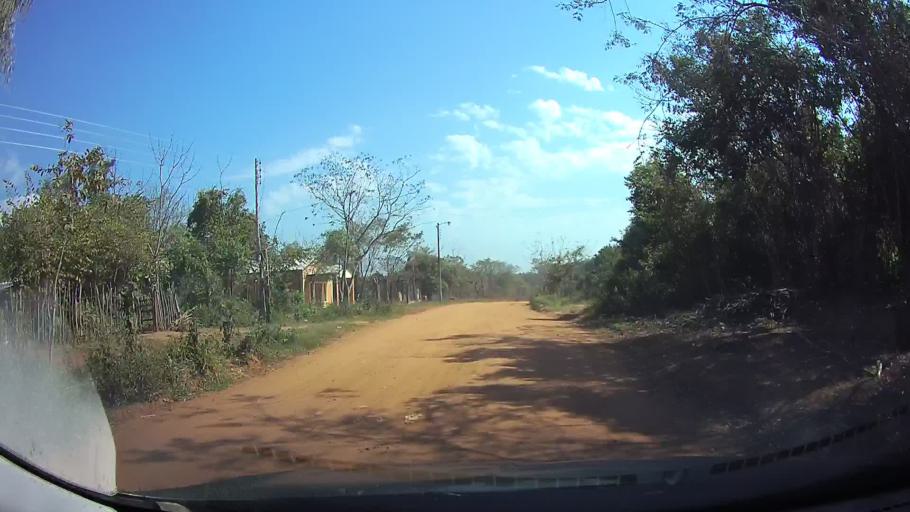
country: PY
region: Central
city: Limpio
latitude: -25.2249
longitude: -57.4364
